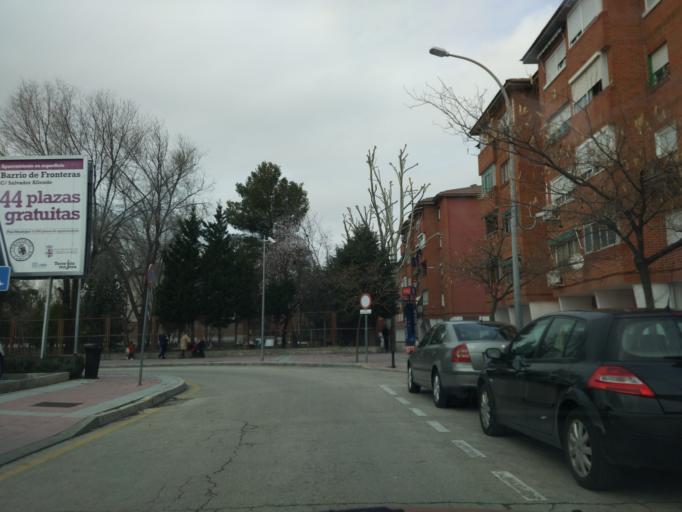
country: ES
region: Madrid
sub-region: Provincia de Madrid
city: Torrejon de Ardoz
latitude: 40.4595
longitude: -3.4861
